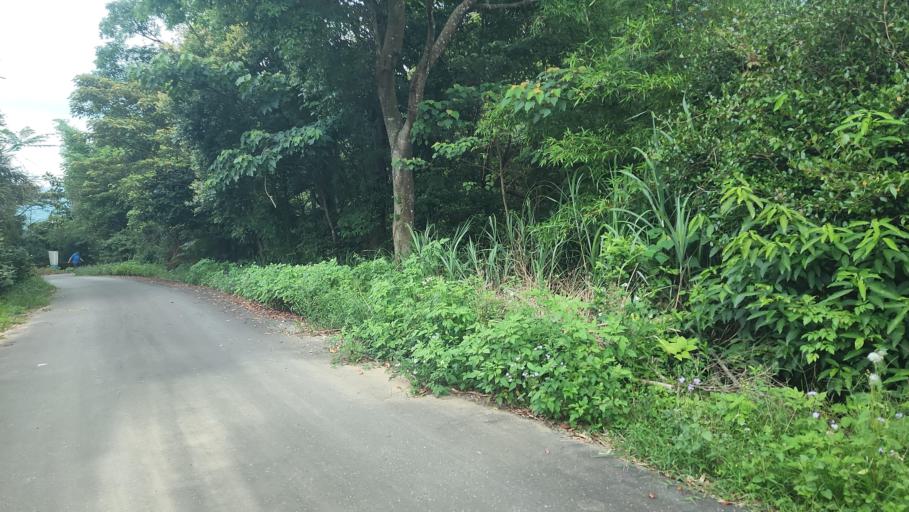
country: TW
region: Taiwan
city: Daxi
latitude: 24.8832
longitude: 121.4197
